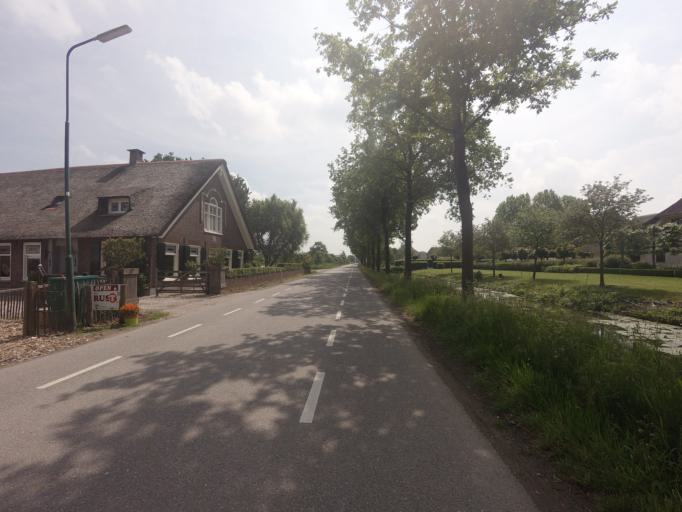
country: NL
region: Utrecht
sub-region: Gemeente Vianen
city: Vianen
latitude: 52.0065
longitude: 5.1237
